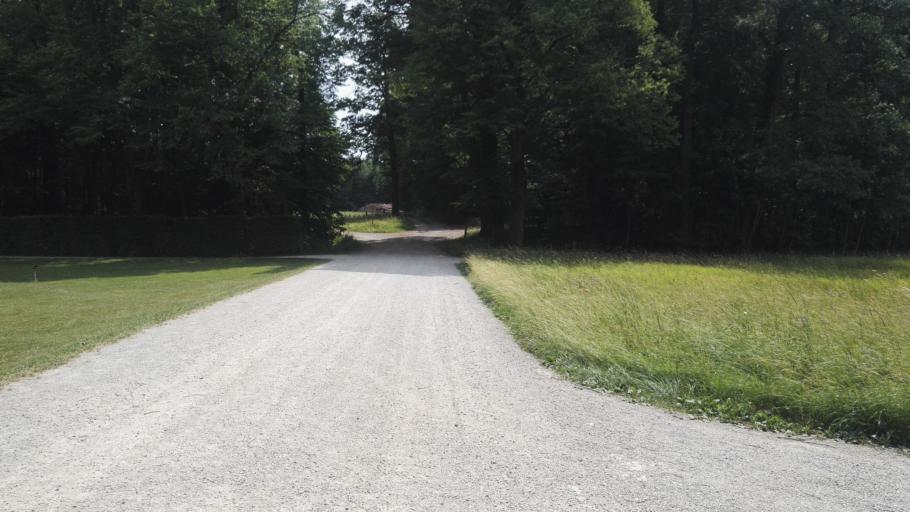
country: DE
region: Bavaria
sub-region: Upper Bavaria
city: Chiemsee
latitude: 47.8613
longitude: 12.3940
